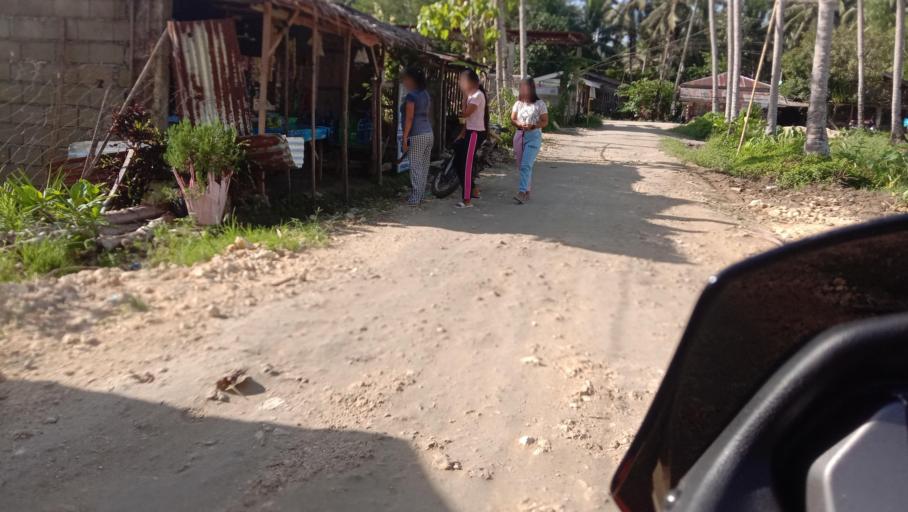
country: PH
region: Caraga
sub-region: Province of Agusan del Sur
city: Alegria
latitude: 8.4811
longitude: 125.9646
